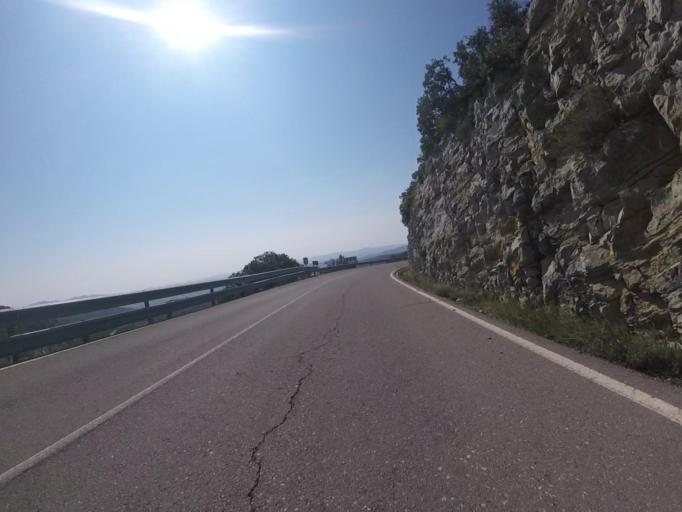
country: ES
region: Valencia
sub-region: Provincia de Castello
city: Benafigos
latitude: 40.2650
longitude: -0.2330
